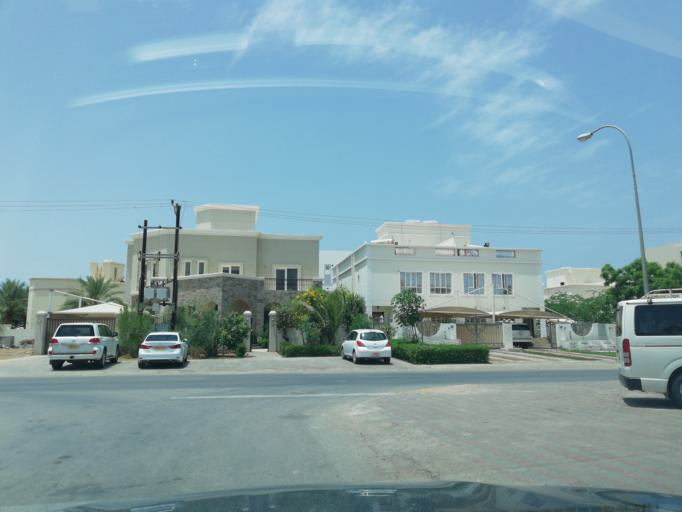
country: OM
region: Muhafazat Masqat
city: As Sib al Jadidah
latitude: 23.6215
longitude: 58.2564
